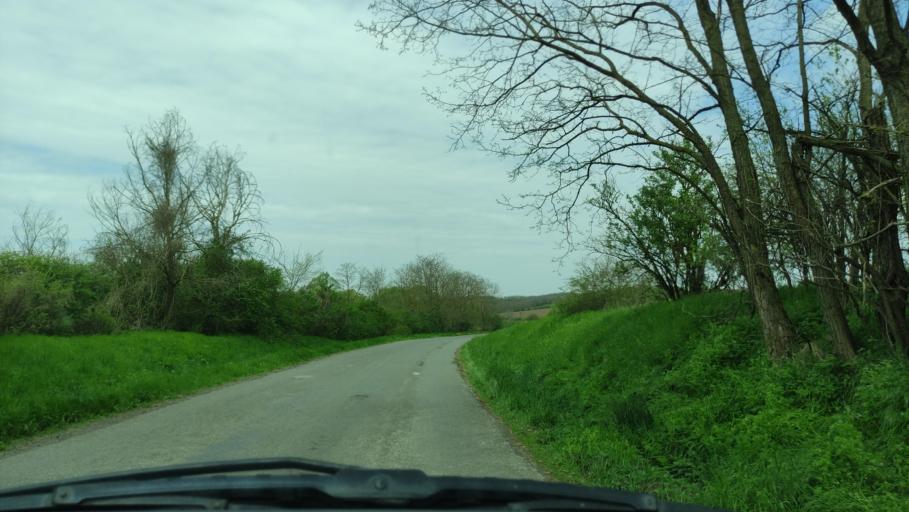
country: HU
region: Baranya
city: Sasd
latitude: 46.3004
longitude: 18.1712
